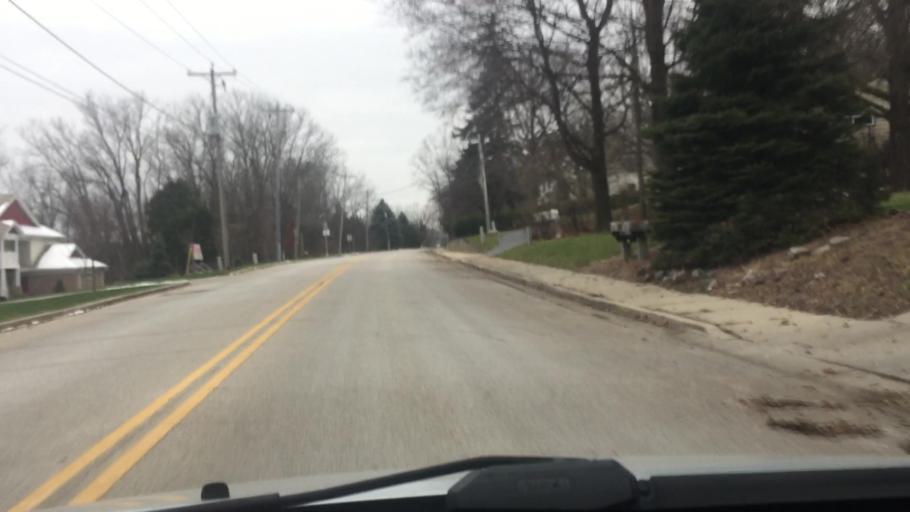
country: US
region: Wisconsin
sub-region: Waukesha County
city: Hartland
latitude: 43.1010
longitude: -88.3564
